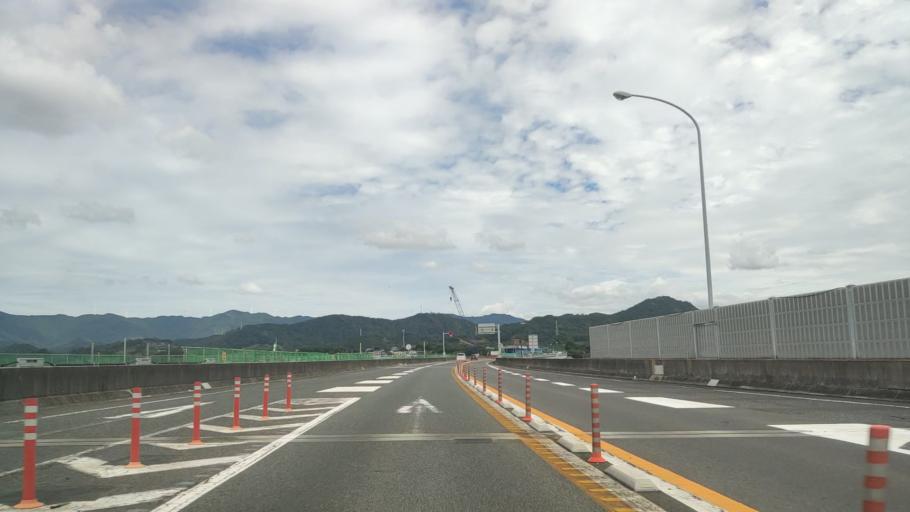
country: JP
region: Wakayama
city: Gobo
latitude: 33.9010
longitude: 135.1863
